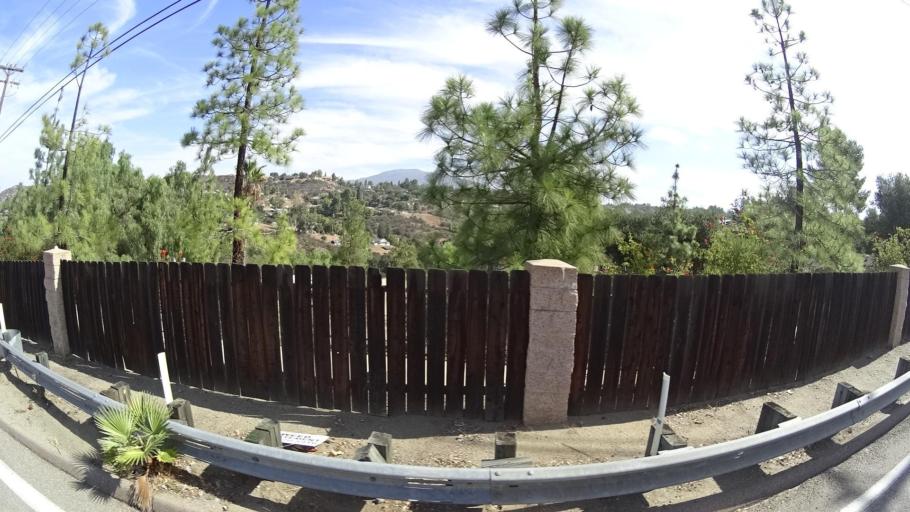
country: US
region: California
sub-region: San Diego County
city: Alpine
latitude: 32.8321
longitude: -116.7983
